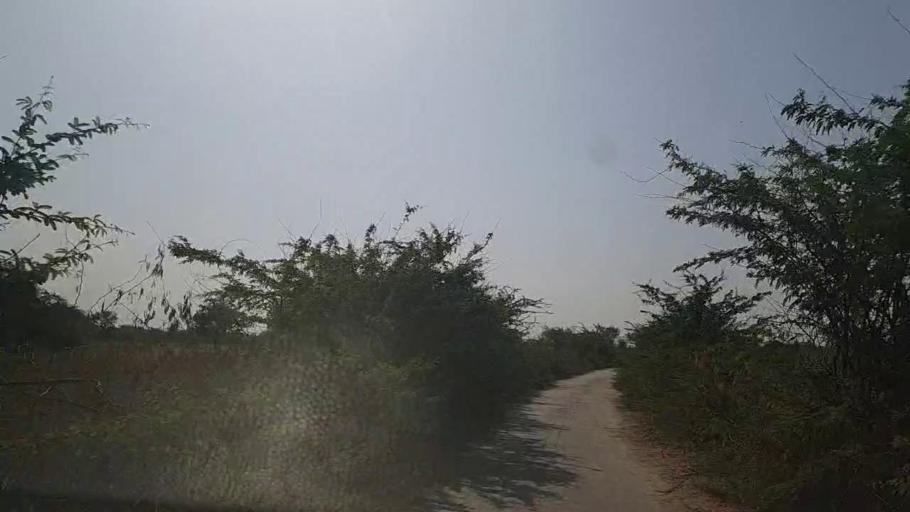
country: PK
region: Sindh
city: Naukot
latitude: 24.5690
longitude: 69.2908
